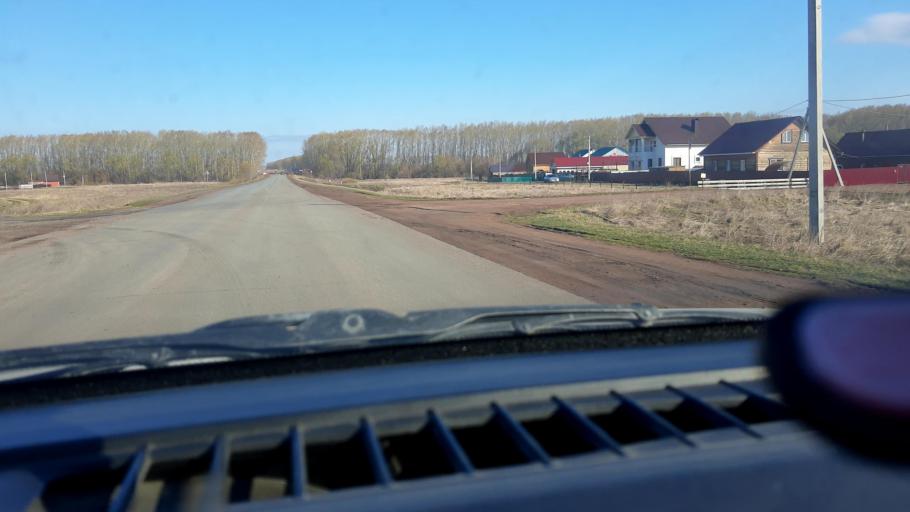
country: RU
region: Bashkortostan
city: Asanovo
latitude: 54.9673
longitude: 55.5424
